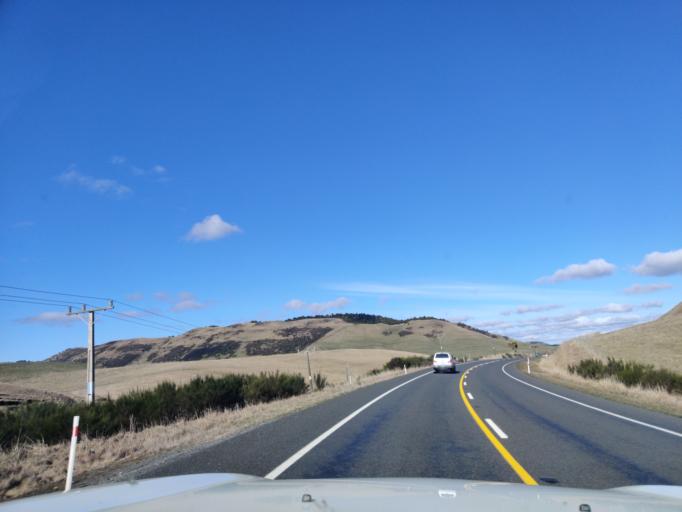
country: NZ
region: Manawatu-Wanganui
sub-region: Ruapehu District
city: Waiouru
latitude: -39.5128
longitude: 175.6837
